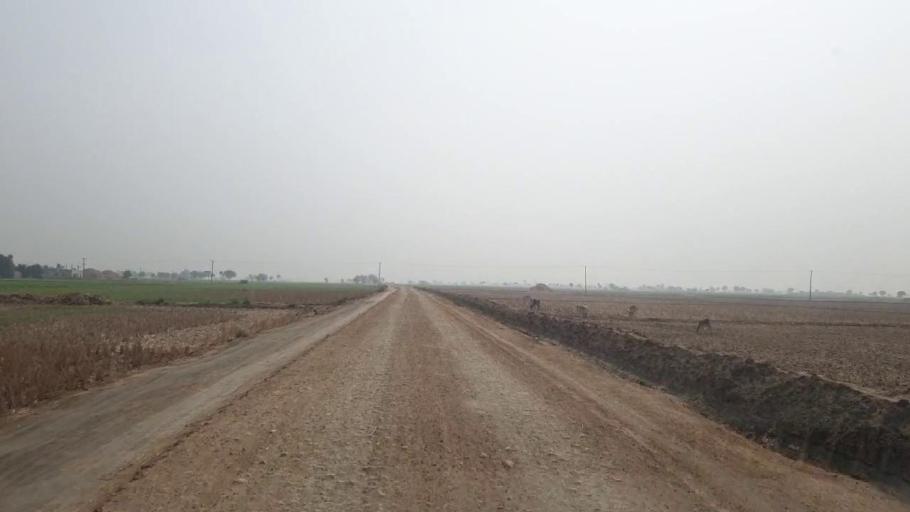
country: PK
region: Sindh
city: Kario
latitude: 24.6492
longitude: 68.5953
